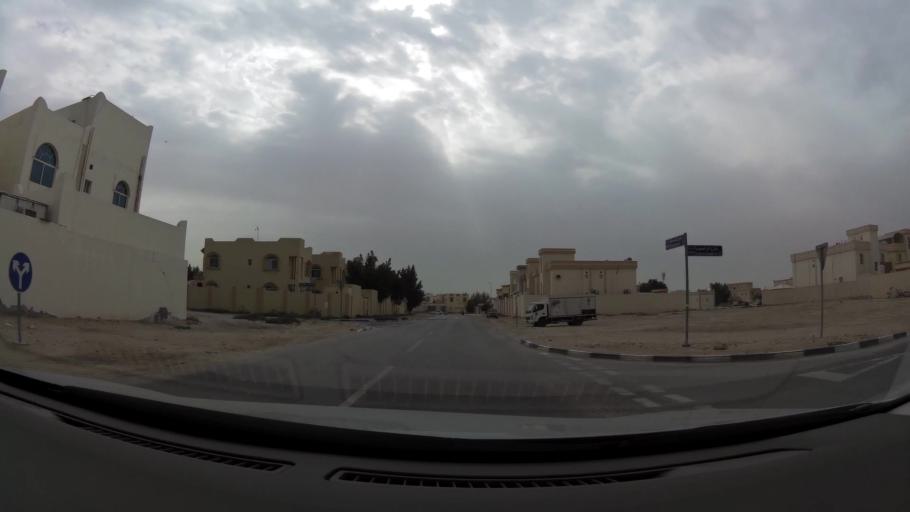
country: QA
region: Baladiyat ar Rayyan
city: Ar Rayyan
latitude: 25.3401
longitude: 51.4740
